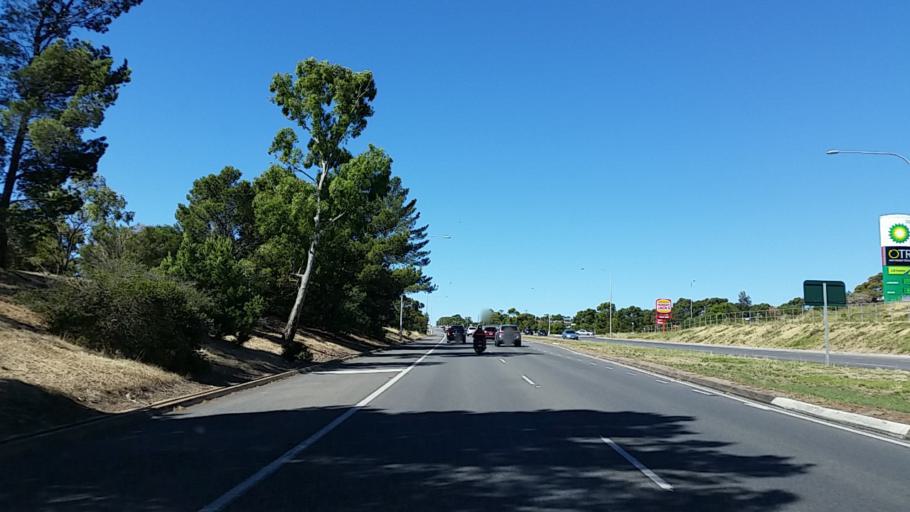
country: AU
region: South Australia
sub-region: Marion
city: Happy Valley
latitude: -35.0761
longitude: 138.5208
